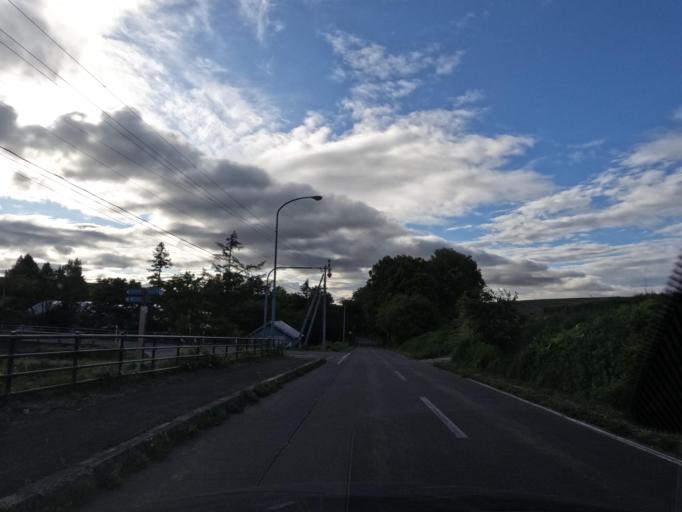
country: JP
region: Hokkaido
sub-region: Asahikawa-shi
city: Asahikawa
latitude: 43.6316
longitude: 142.4349
